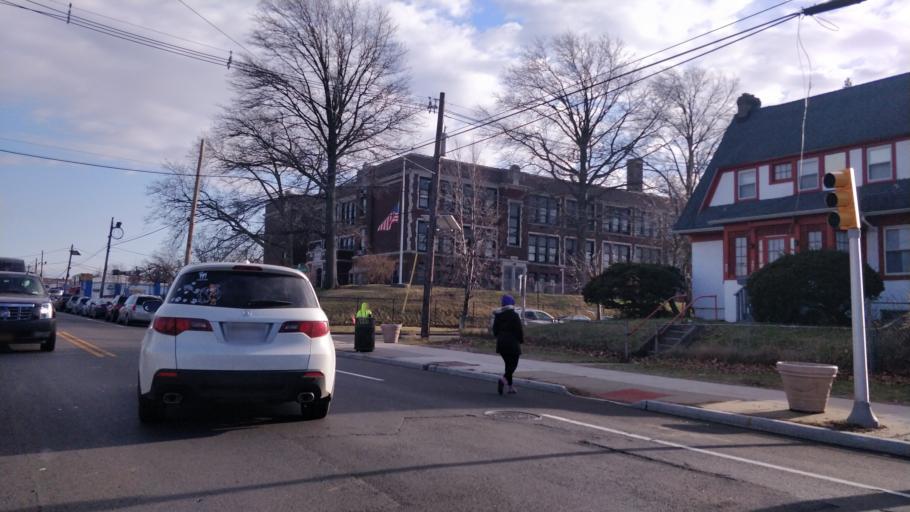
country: US
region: New Jersey
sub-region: Union County
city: Elizabeth
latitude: 40.6474
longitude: -74.2165
